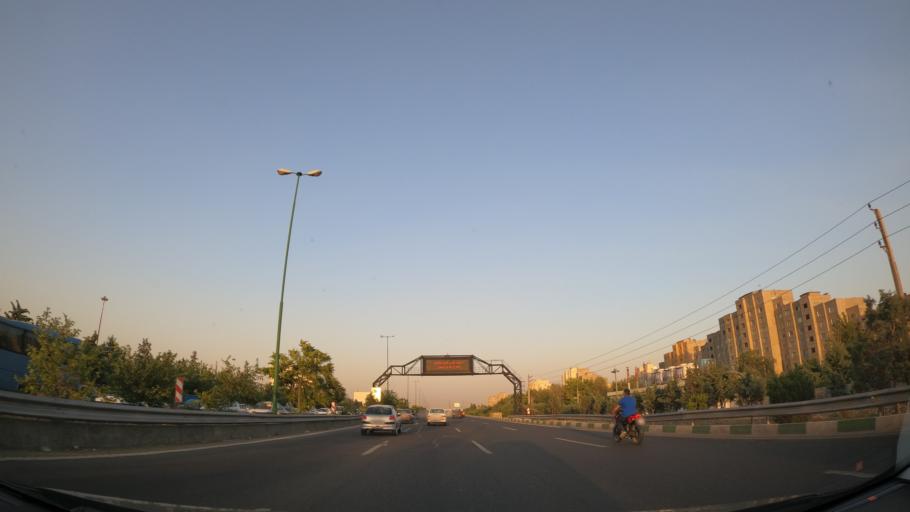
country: IR
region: Tehran
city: Tehran
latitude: 35.7153
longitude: 51.3210
